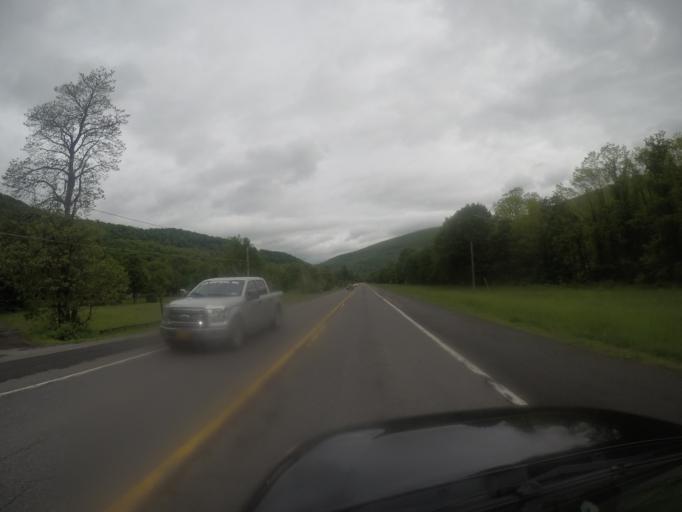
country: US
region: New York
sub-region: Ulster County
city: Shokan
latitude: 42.0658
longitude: -74.3076
